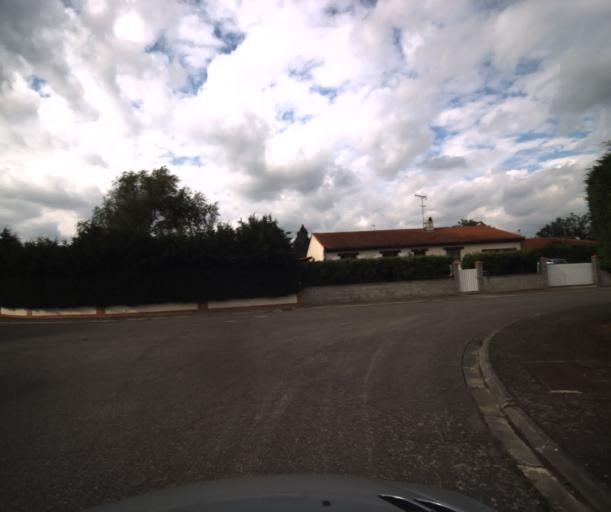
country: FR
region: Midi-Pyrenees
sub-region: Departement de la Haute-Garonne
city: Labarthe-sur-Leze
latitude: 43.4498
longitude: 1.4001
